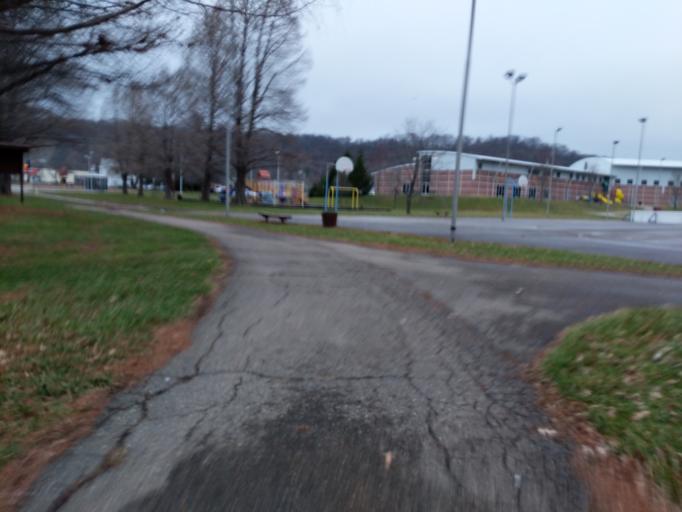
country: US
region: Ohio
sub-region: Athens County
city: Athens
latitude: 39.3360
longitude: -82.0769
